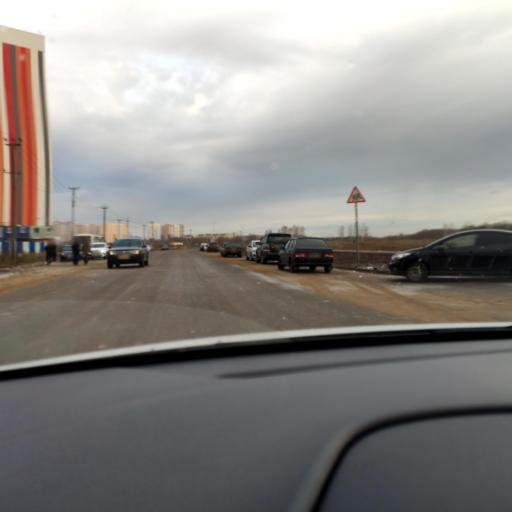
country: RU
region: Tatarstan
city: Osinovo
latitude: 55.8598
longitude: 48.9009
